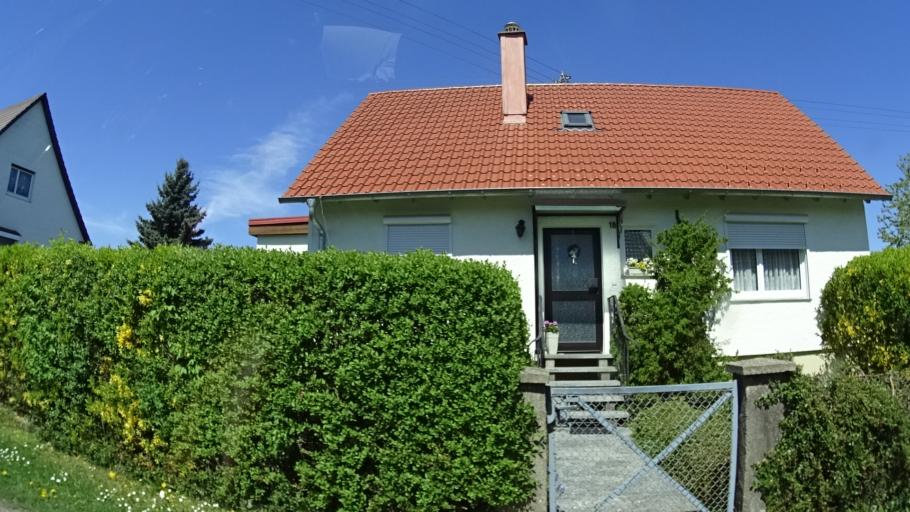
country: DE
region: Baden-Wuerttemberg
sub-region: Freiburg Region
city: Zimmern ob Rottweil
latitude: 48.1694
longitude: 8.5802
